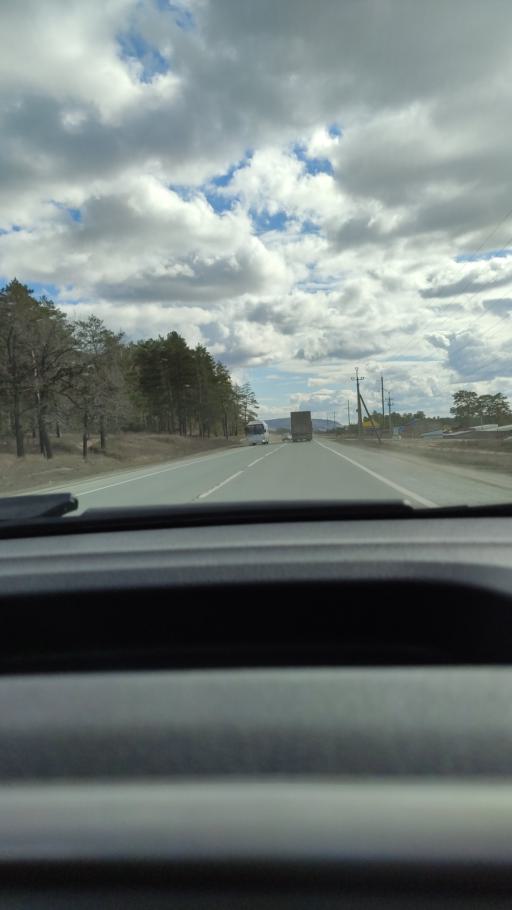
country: RU
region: Samara
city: Kurumoch
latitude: 53.4626
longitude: 50.0776
